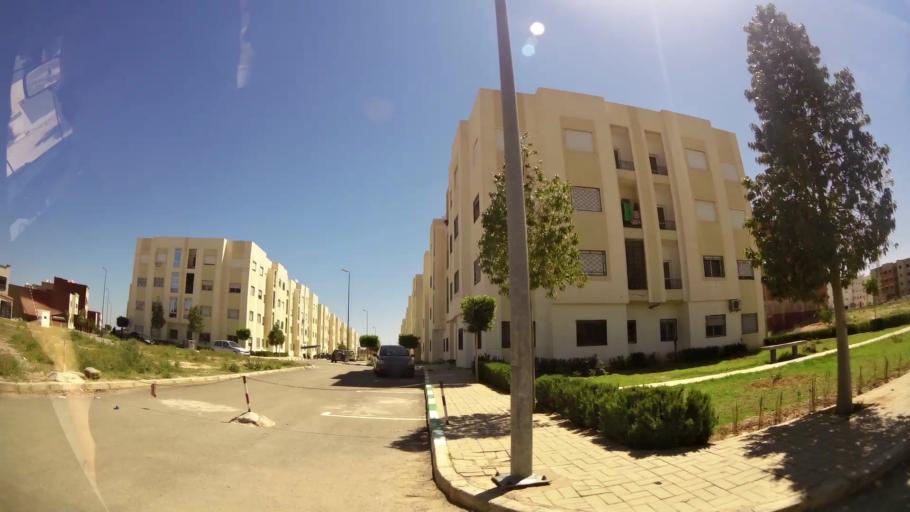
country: MA
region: Oriental
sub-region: Oujda-Angad
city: Oujda
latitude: 34.6555
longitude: -1.8832
